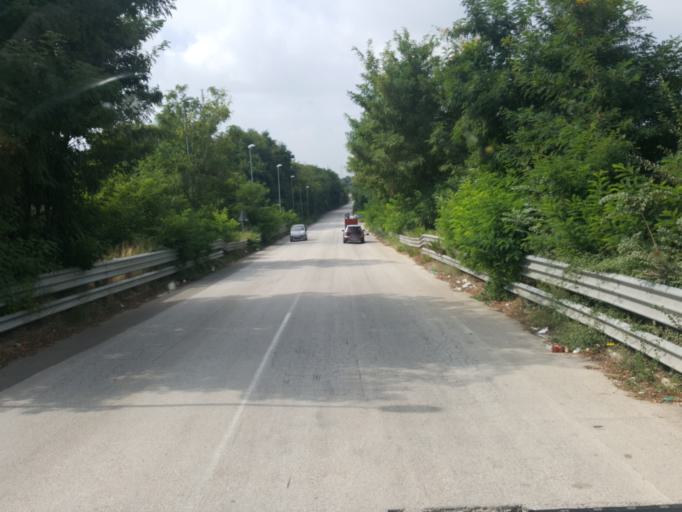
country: IT
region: Campania
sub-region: Provincia di Caserta
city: Pignataro Maggiore
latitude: 41.1784
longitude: 14.1541
